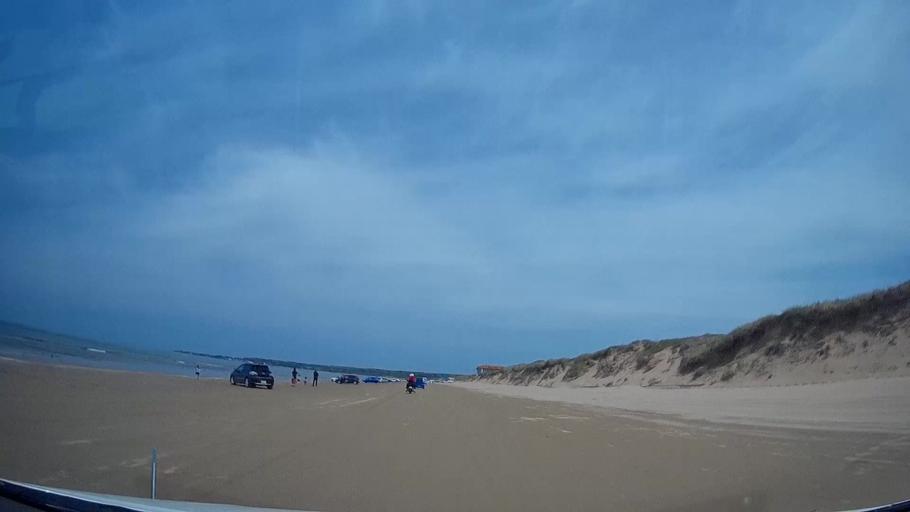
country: JP
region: Ishikawa
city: Hakui
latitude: 36.8895
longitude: 136.7646
